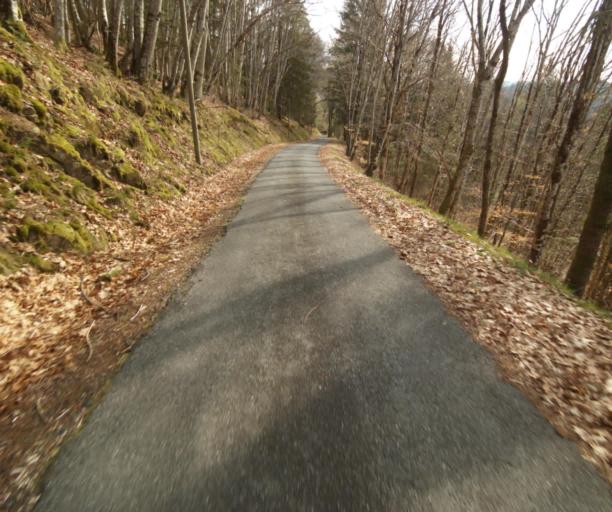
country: FR
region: Limousin
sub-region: Departement de la Correze
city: Correze
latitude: 45.3633
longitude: 1.8594
